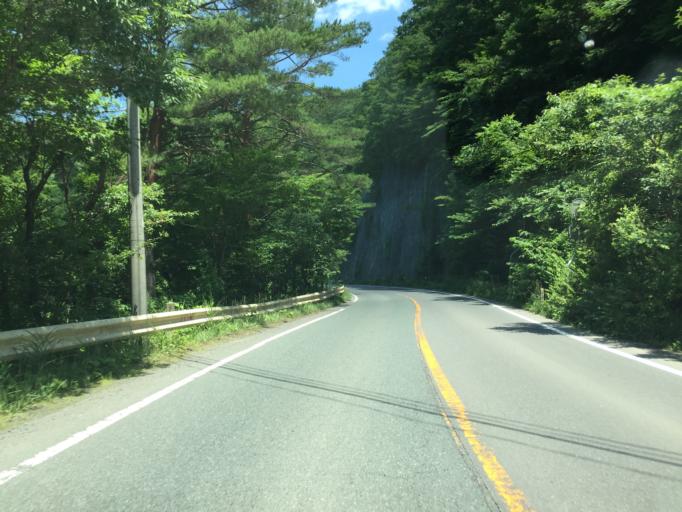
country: JP
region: Miyagi
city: Marumori
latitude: 37.7731
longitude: 140.7668
